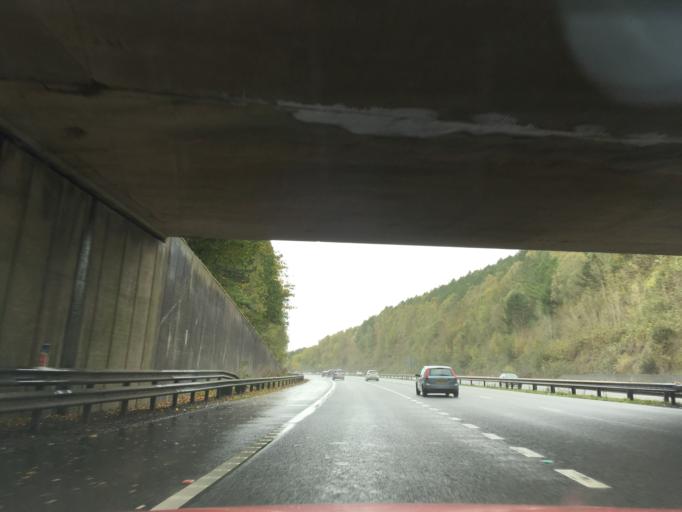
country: GB
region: Wales
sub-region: Cardiff
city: Radyr
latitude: 51.5326
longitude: -3.2261
